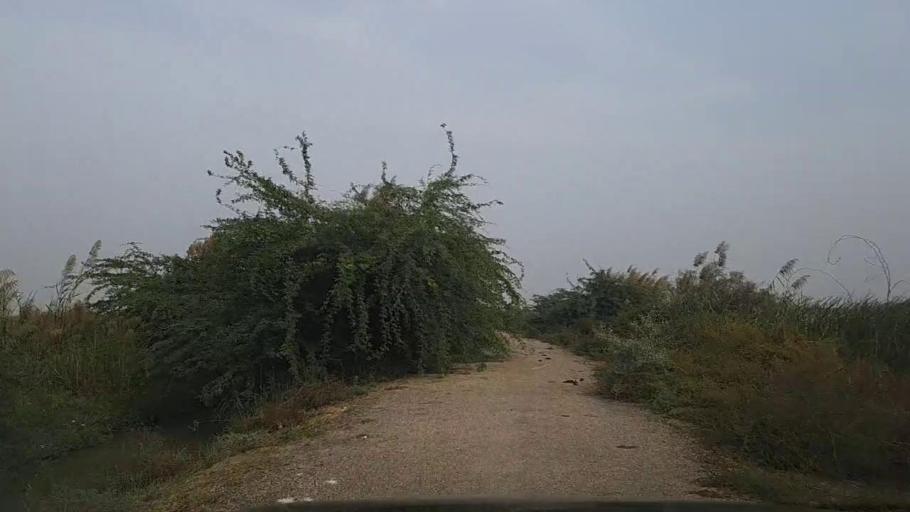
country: PK
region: Sindh
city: Chuhar Jamali
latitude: 24.5054
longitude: 67.8965
